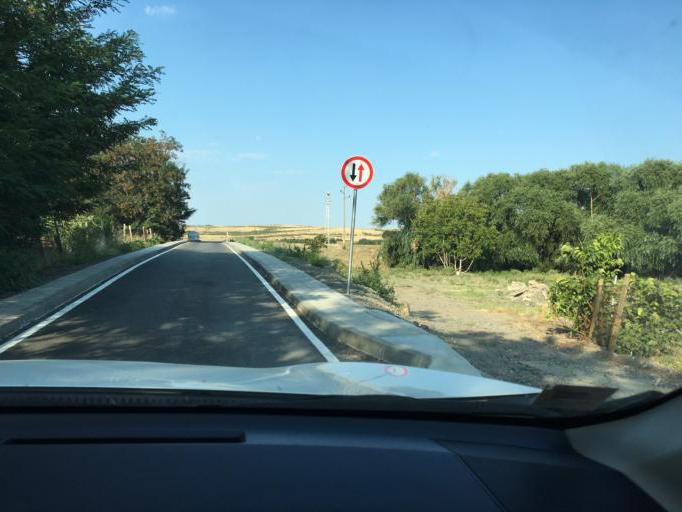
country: BG
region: Burgas
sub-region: Obshtina Burgas
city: Burgas
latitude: 42.6115
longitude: 27.4818
